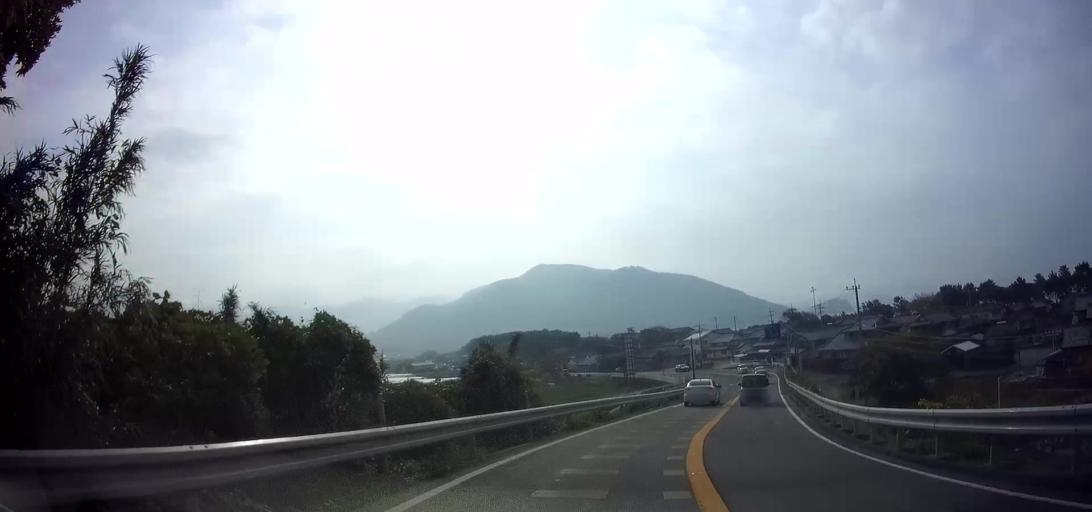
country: JP
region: Nagasaki
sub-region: Isahaya-shi
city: Isahaya
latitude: 32.7944
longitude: 130.1832
